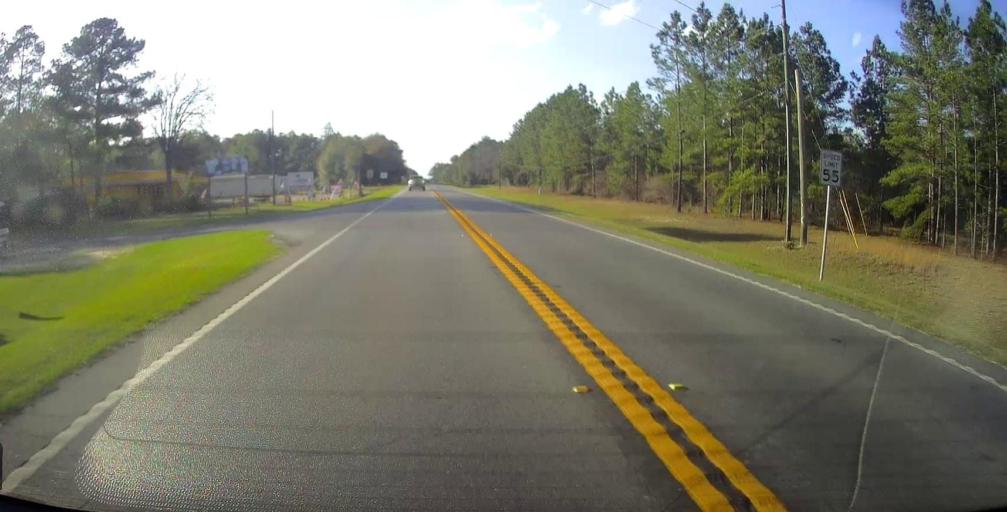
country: US
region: Georgia
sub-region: Tattnall County
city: Reidsville
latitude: 32.0829
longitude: -82.1363
